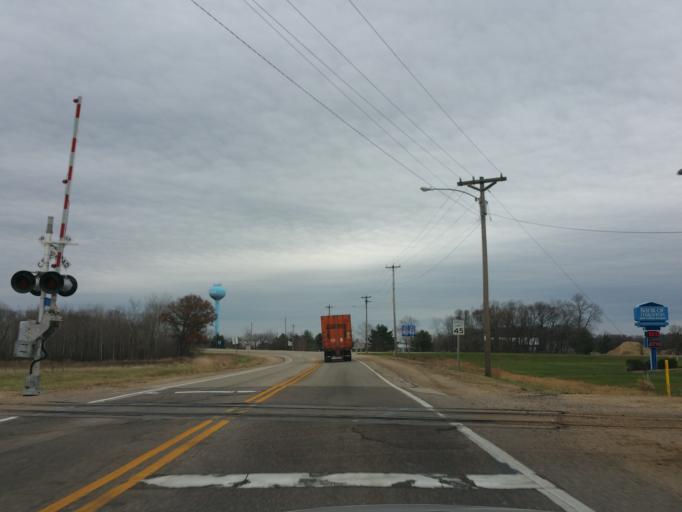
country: US
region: Wisconsin
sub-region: Juneau County
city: New Lisbon
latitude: 43.8810
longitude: -90.1549
